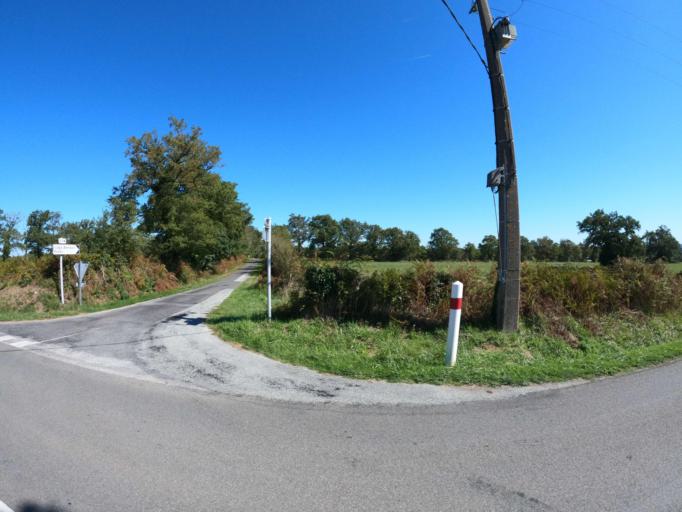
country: FR
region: Limousin
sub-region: Departement de la Haute-Vienne
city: Le Dorat
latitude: 46.2457
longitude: 1.0495
